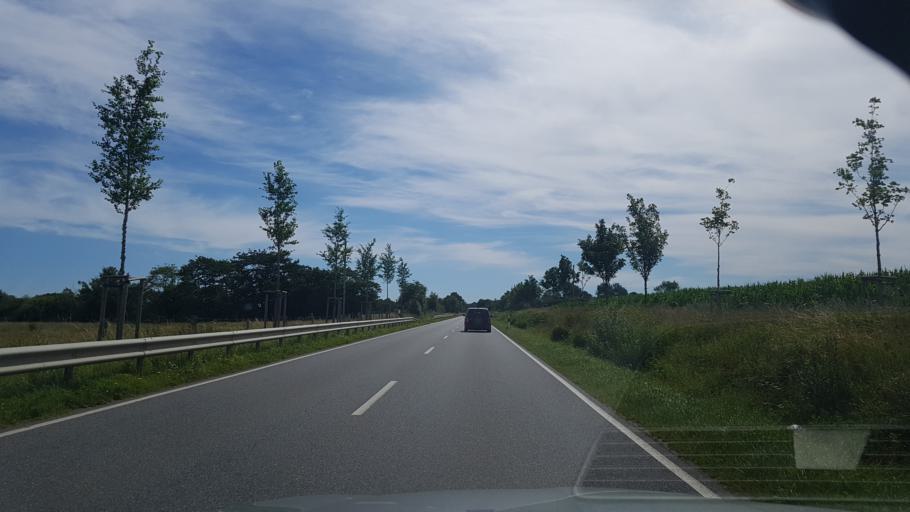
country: DE
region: Schleswig-Holstein
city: Wallsbull
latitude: 54.7978
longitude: 9.2822
